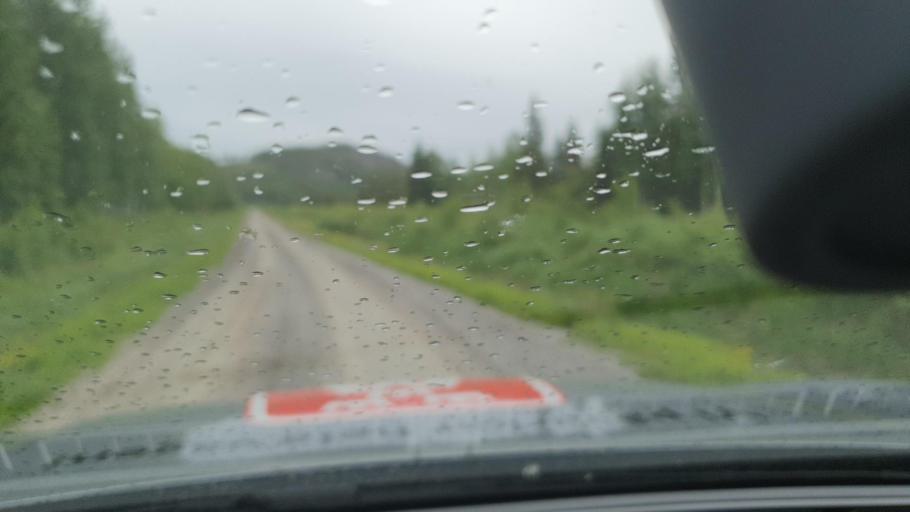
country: SE
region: Norrbotten
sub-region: Kalix Kommun
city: Rolfs
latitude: 66.0652
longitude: 22.9990
